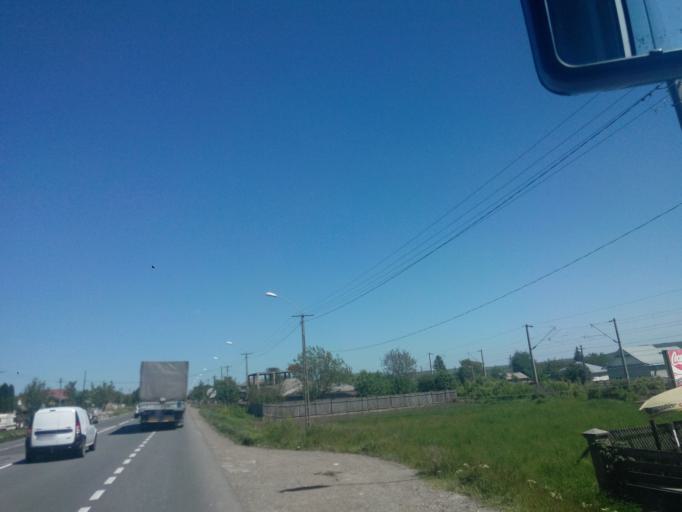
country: RO
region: Iasi
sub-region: Comuna Podu Iloaiei
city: Budai
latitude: 47.2182
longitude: 27.2249
